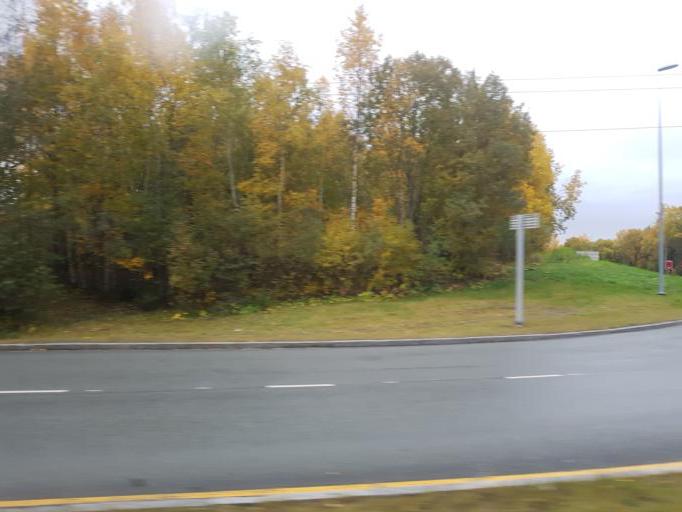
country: NO
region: Sor-Trondelag
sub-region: Trondheim
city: Trondheim
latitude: 63.3716
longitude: 10.3462
